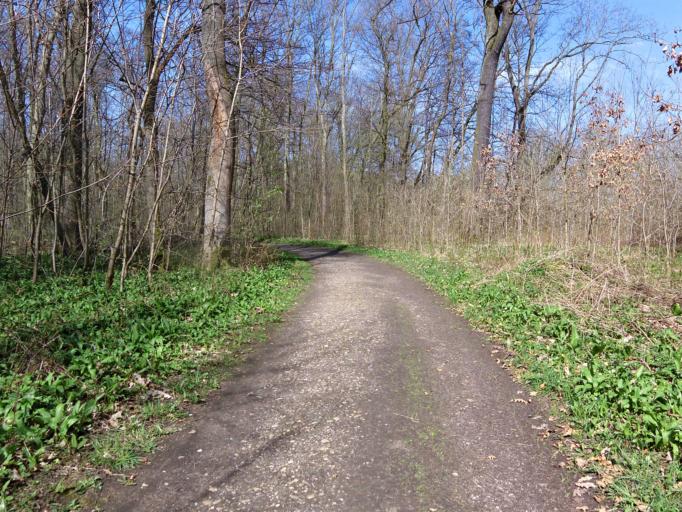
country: DE
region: Saxony
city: Schkeuditz
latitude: 51.3760
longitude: 12.2875
